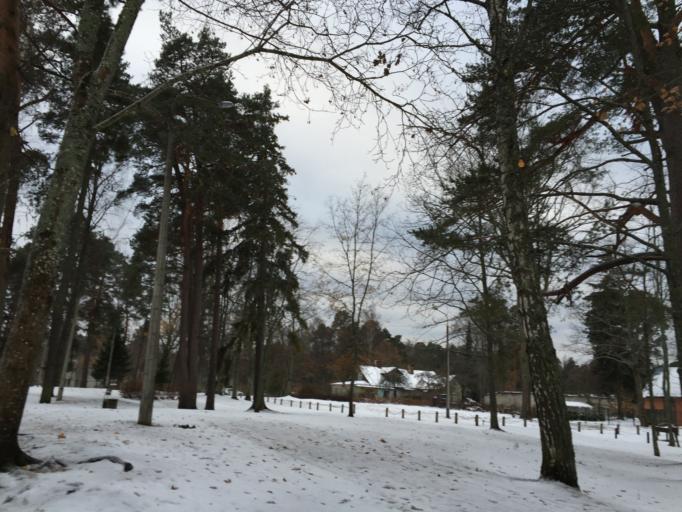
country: LV
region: Saulkrastu
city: Saulkrasti
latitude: 57.2765
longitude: 24.4188
